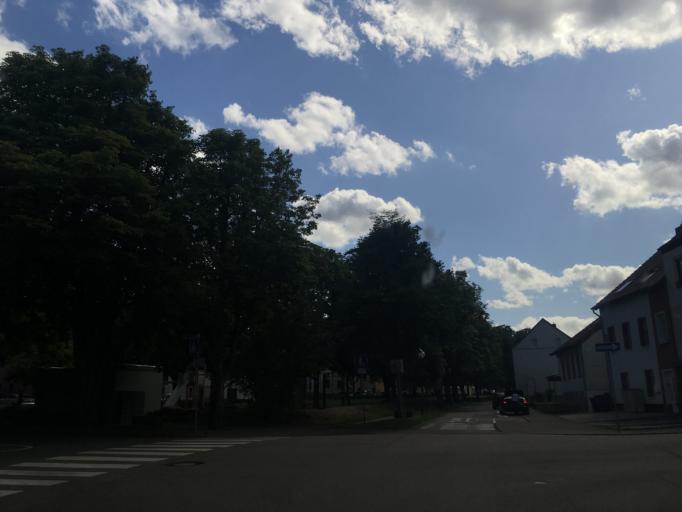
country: DE
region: Saarland
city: Sankt Ingbert
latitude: 49.2756
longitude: 7.1195
